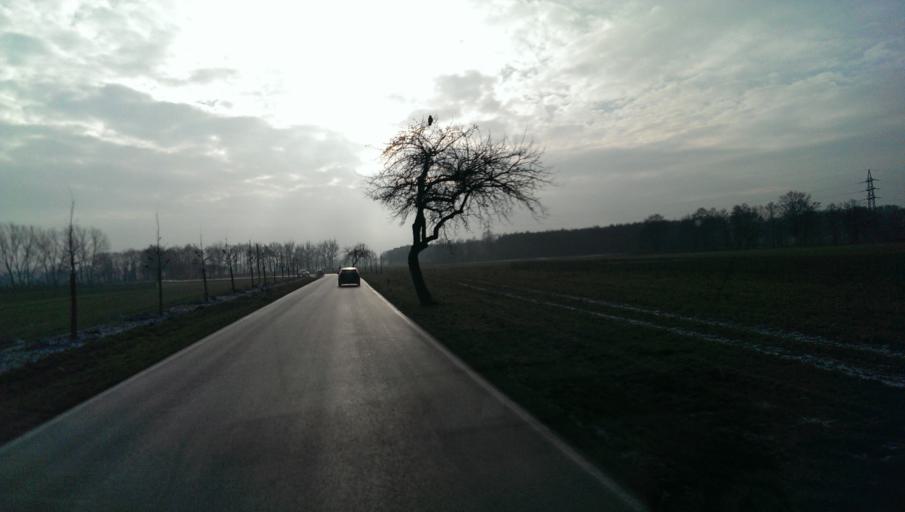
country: DE
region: Saxony
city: Nauwalde
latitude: 51.4325
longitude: 13.4625
